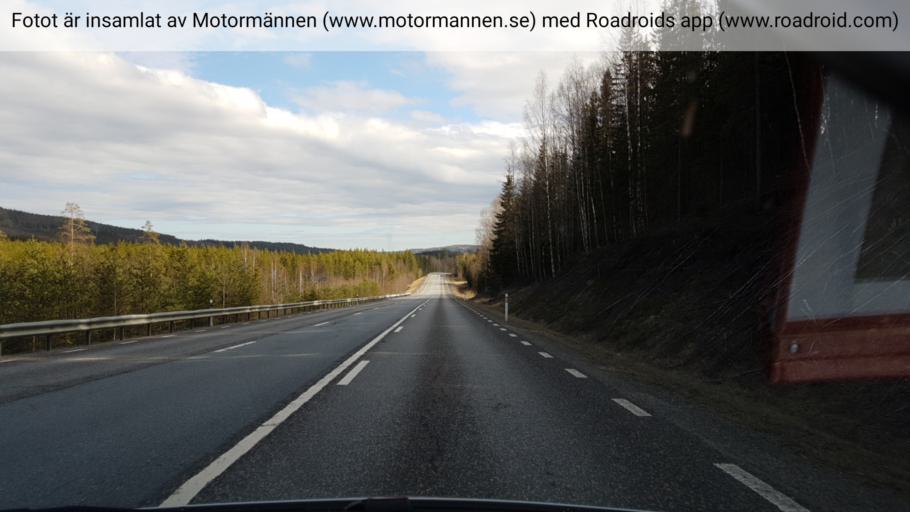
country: SE
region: Vaesternorrland
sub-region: Kramfors Kommun
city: Bollstabruk
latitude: 63.1104
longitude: 17.5022
